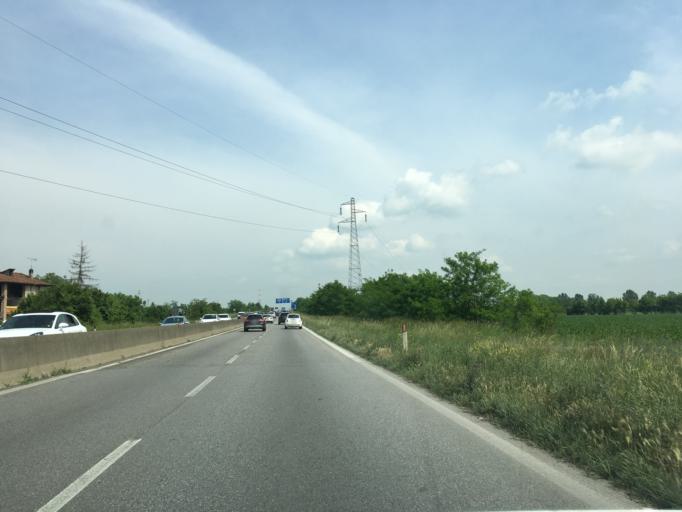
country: IT
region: Lombardy
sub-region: Provincia di Brescia
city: Rezzato
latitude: 45.4981
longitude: 10.3051
